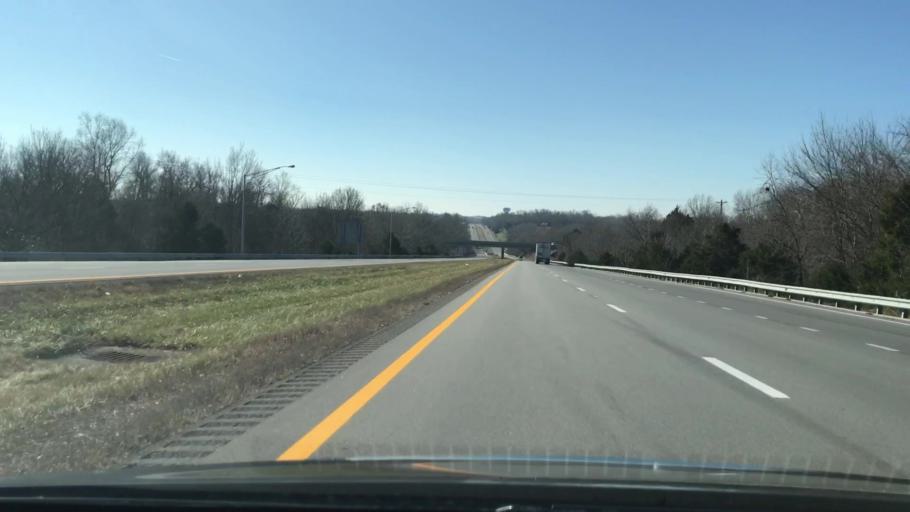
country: US
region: Kentucky
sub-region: Adair County
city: Columbia
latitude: 37.0856
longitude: -85.3075
